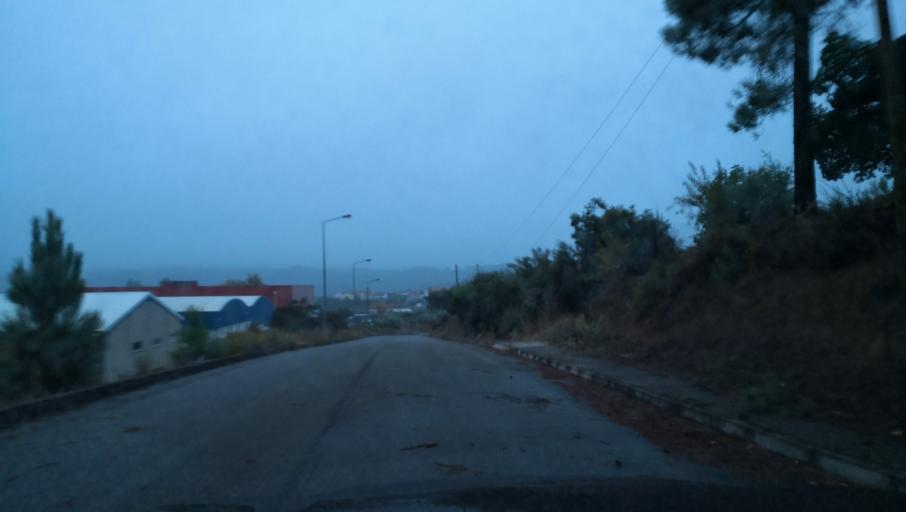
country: PT
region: Vila Real
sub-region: Sabrosa
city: Sabrosa
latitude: 41.2669
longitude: -7.5903
